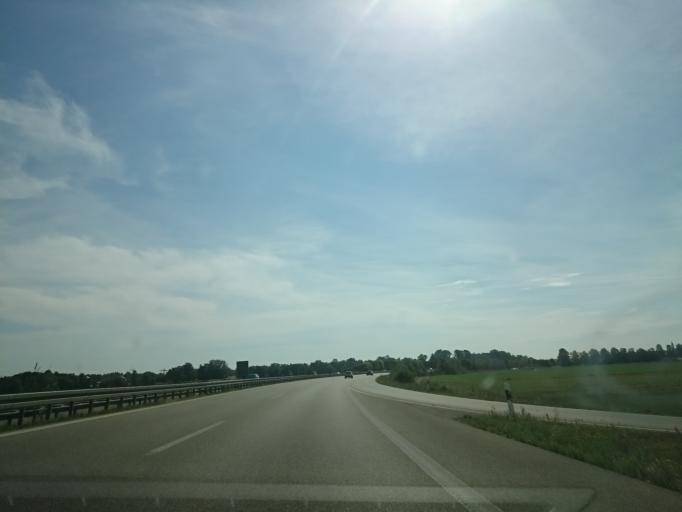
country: DE
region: Bavaria
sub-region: Swabia
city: Langweid
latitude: 48.5022
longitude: 10.8578
